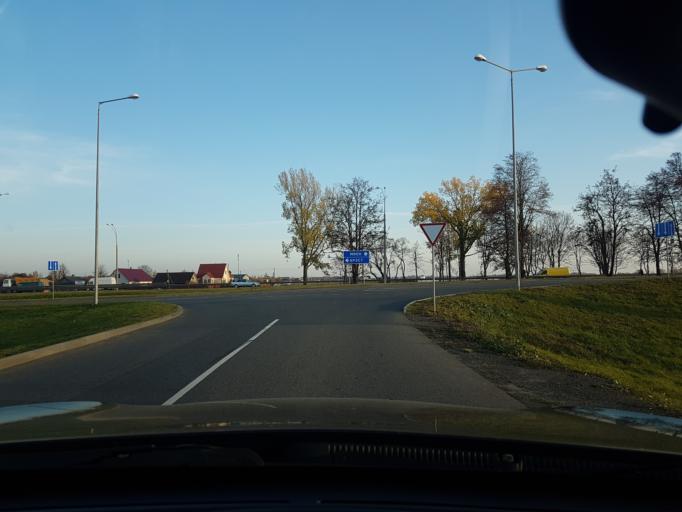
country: BY
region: Minsk
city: Shchomyslitsa
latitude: 53.8208
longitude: 27.4355
